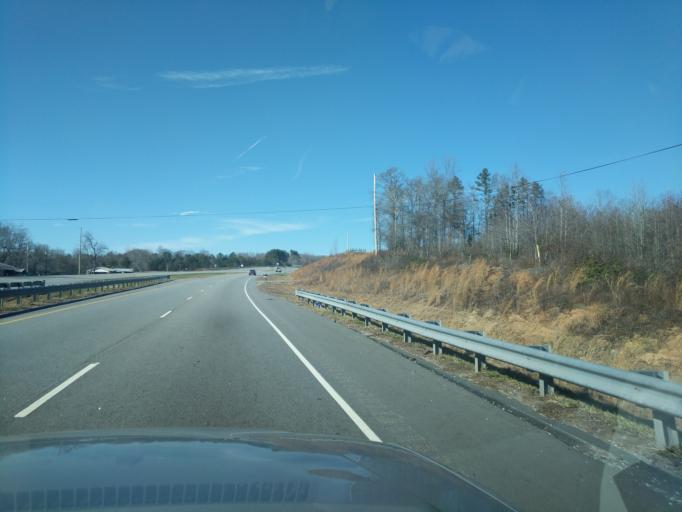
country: US
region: North Carolina
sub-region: Rutherford County
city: Forest City
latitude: 35.2457
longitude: -81.8667
